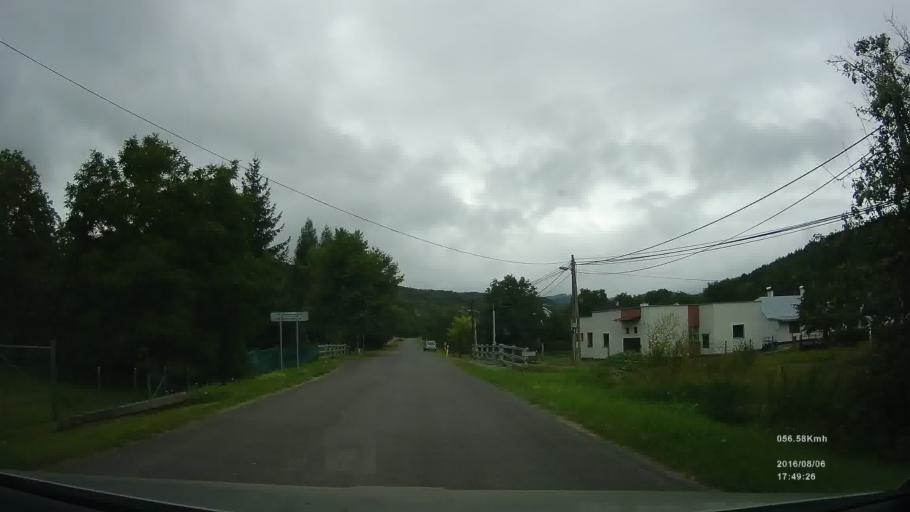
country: SK
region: Presovsky
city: Svidnik
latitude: 49.3834
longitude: 21.5695
